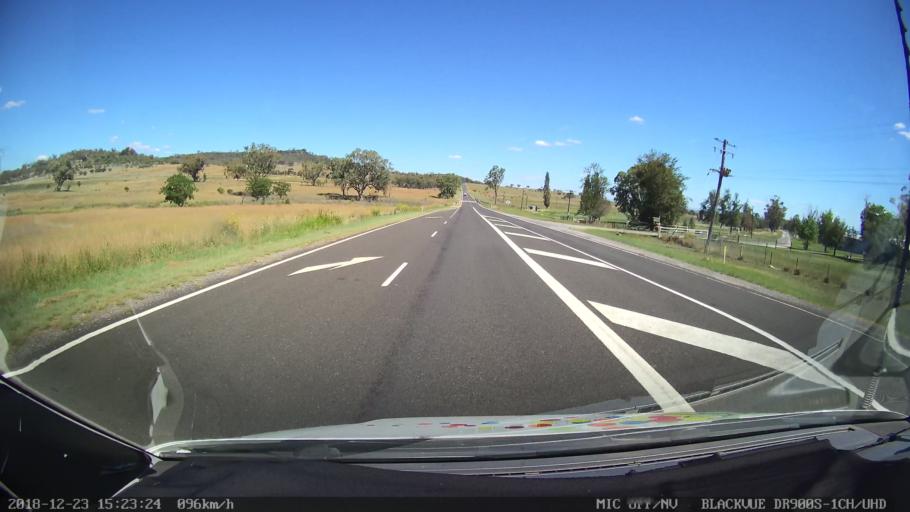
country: AU
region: New South Wales
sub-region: Tamworth Municipality
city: Manilla
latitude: -30.8796
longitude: 150.8136
